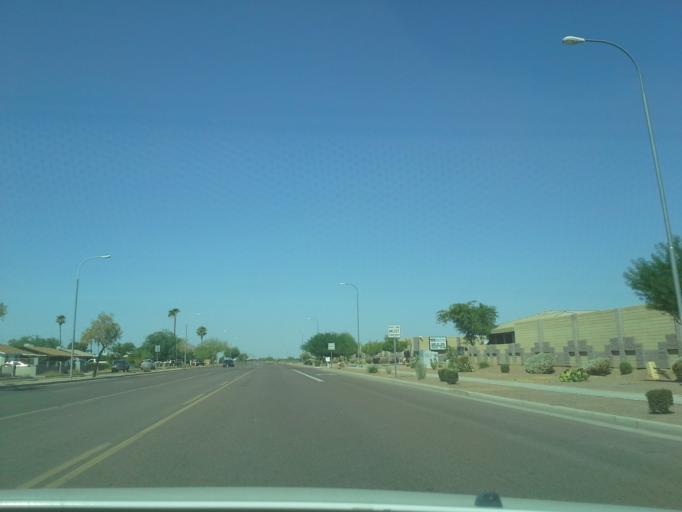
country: US
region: Arizona
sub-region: Maricopa County
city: Laveen
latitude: 33.4068
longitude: -112.1353
